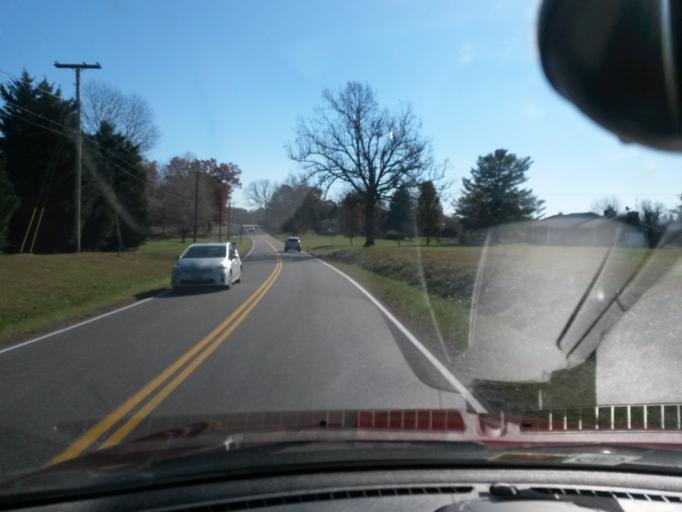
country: US
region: Virginia
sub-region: City of Bedford
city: Bedford
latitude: 37.3741
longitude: -79.5449
